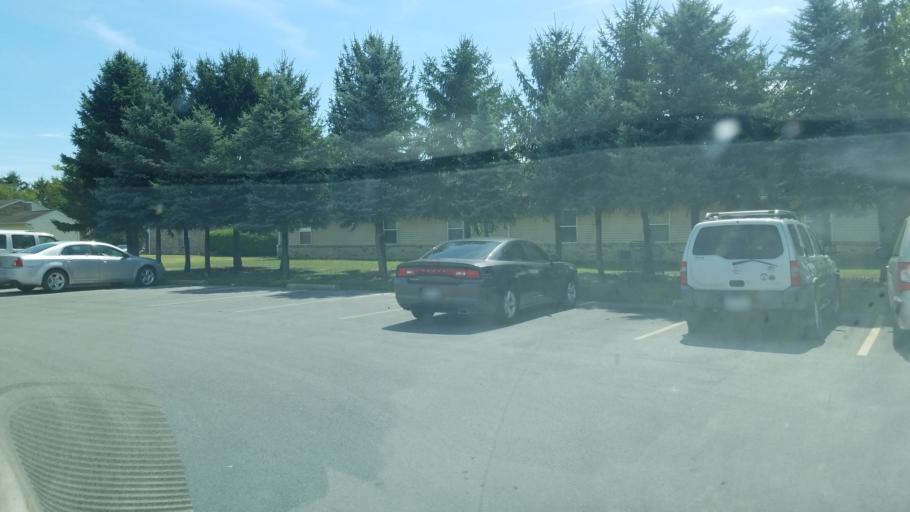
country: US
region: Ohio
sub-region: Hardin County
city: Kenton
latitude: 40.6568
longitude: -83.5925
